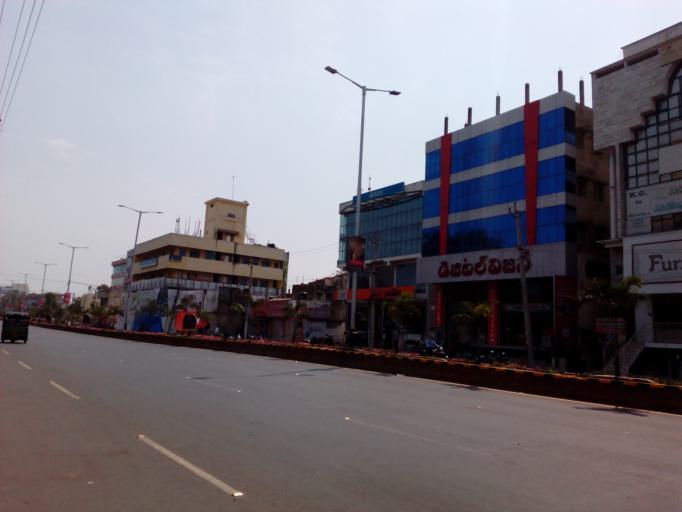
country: IN
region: Andhra Pradesh
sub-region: Krishna
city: Vijayawada
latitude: 16.5031
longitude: 80.6346
